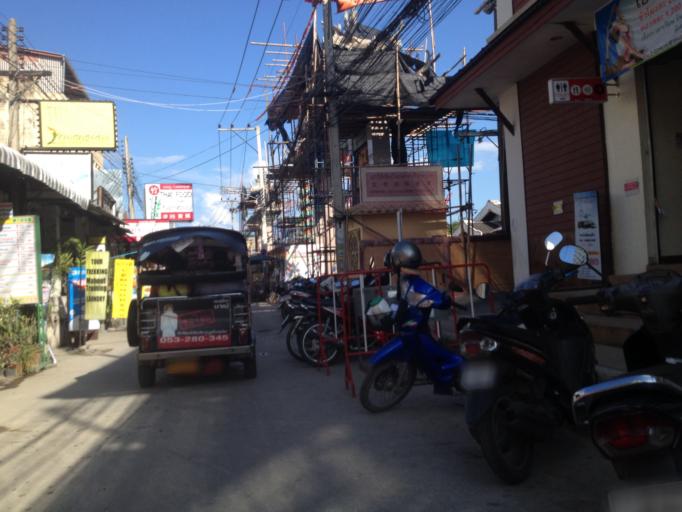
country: TH
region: Chiang Mai
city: Chiang Mai
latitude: 18.7839
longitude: 99.0010
